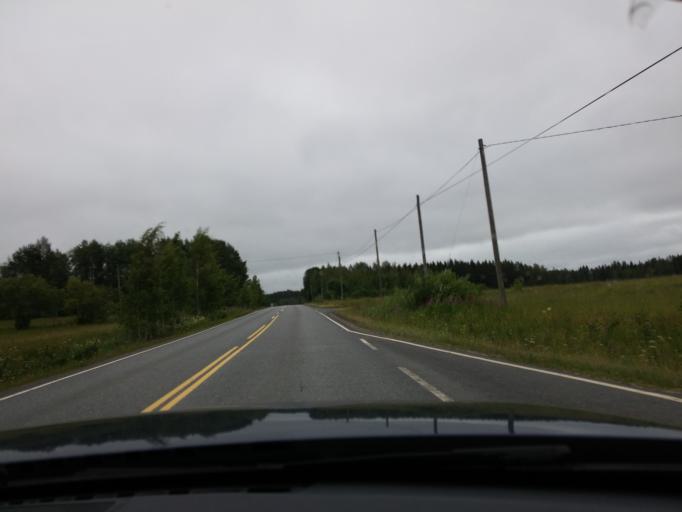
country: FI
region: Central Finland
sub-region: Joutsa
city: Joutsa
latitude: 61.7858
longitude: 26.0417
